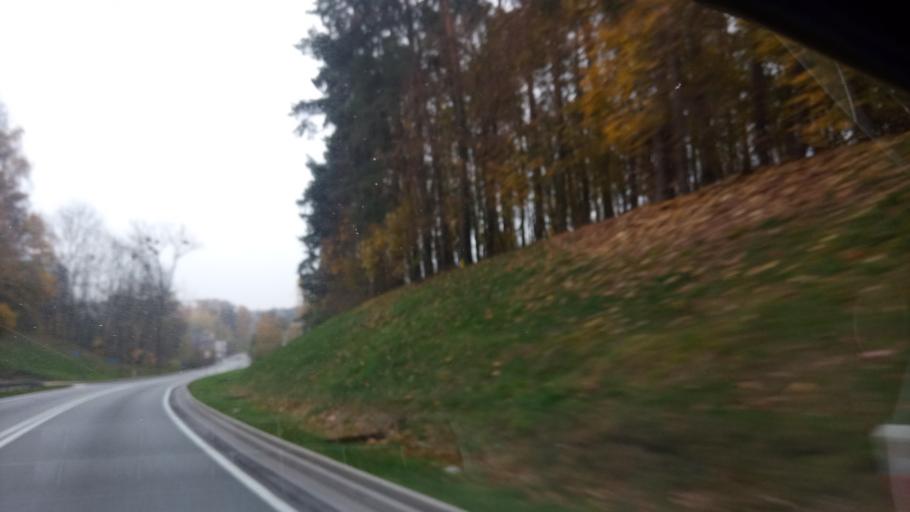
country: PL
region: Kujawsko-Pomorskie
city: Kamien Krajenski
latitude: 53.5389
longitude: 17.5208
